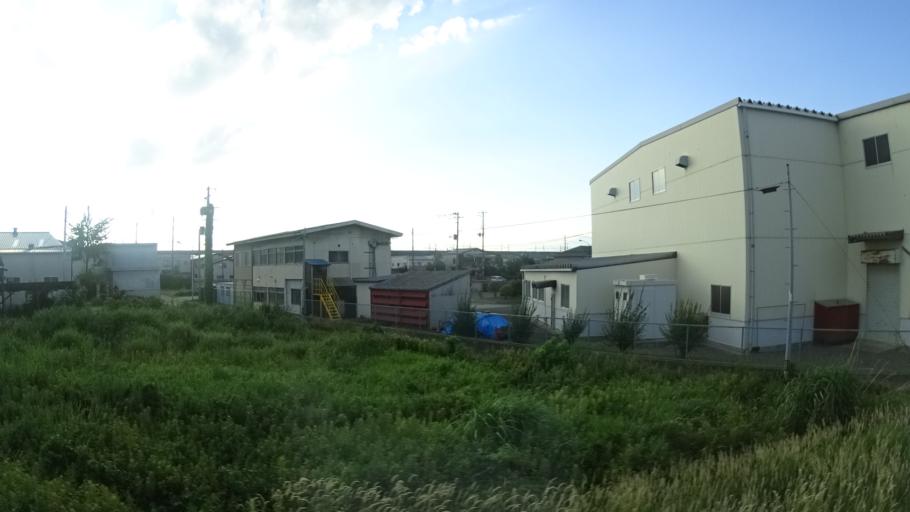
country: JP
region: Fukushima
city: Koriyama
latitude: 37.4124
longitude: 140.3977
